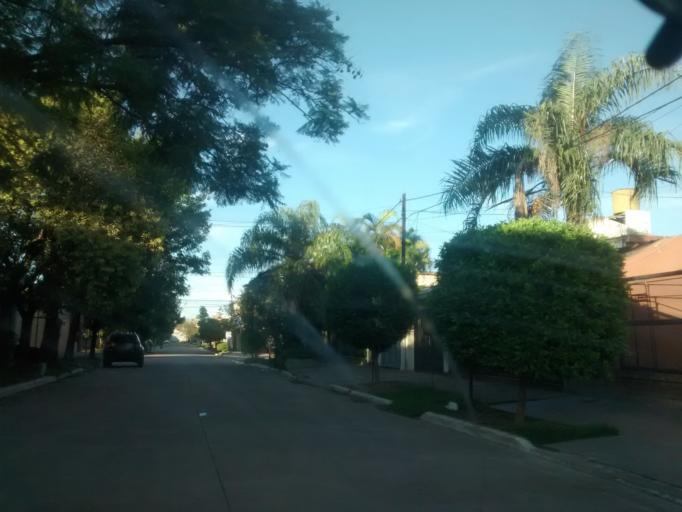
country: AR
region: Chaco
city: Resistencia
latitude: -27.4614
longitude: -58.9705
